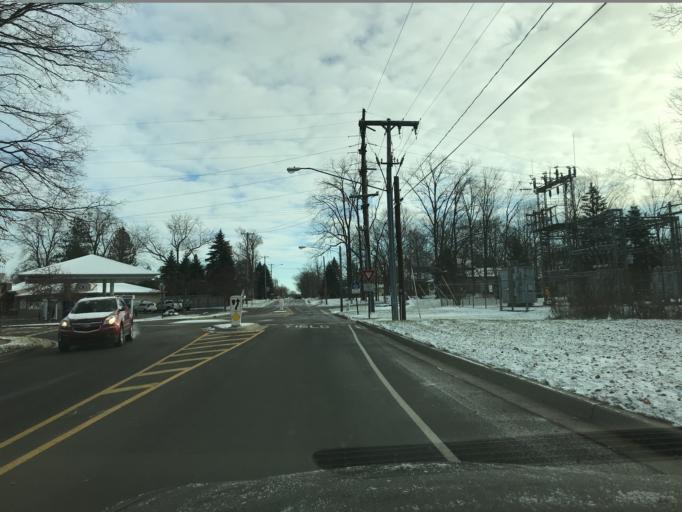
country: US
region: Michigan
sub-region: Eaton County
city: Dimondale
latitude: 42.6474
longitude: -84.6432
